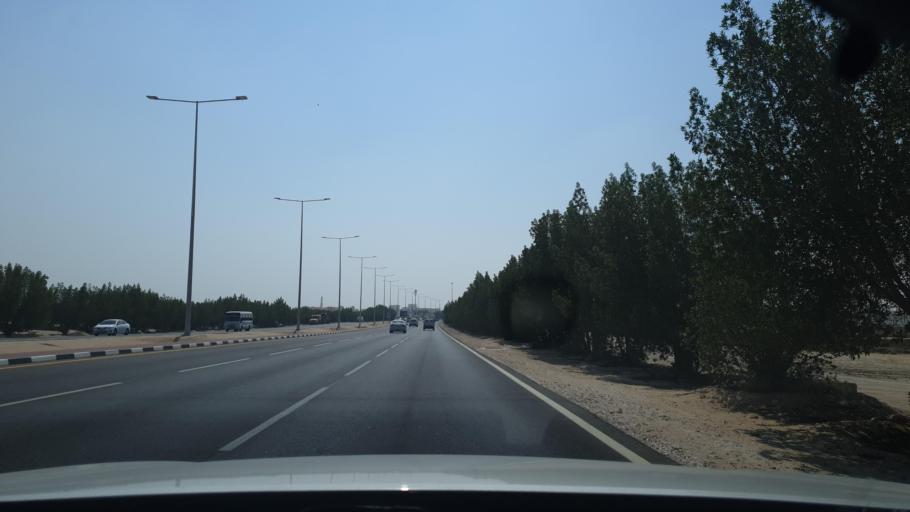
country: QA
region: Al Khawr
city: Al Khawr
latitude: 25.6959
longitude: 51.5015
